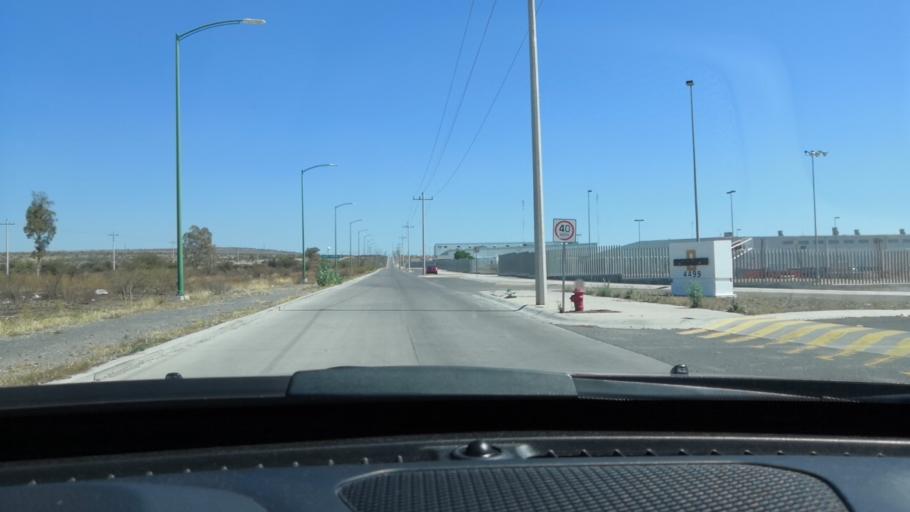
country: MX
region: Guanajuato
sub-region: Leon
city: Centro Familiar la Soledad
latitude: 21.1031
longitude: -101.7705
